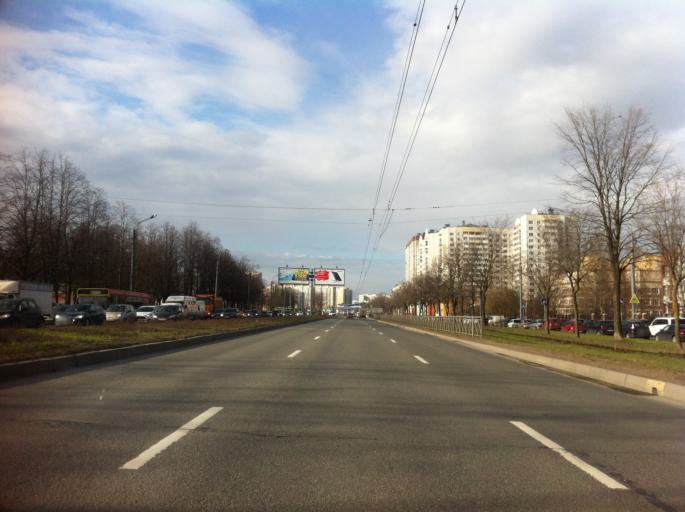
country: RU
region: St.-Petersburg
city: Uritsk
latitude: 59.8484
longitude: 30.1757
